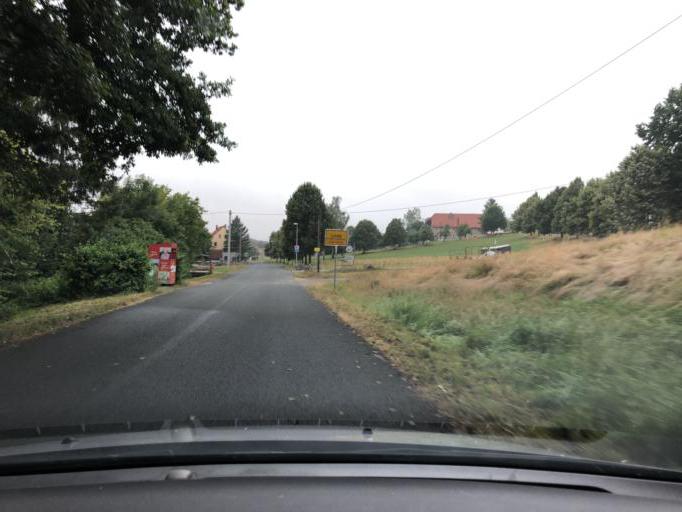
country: DE
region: Thuringia
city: Langenleuba-Niederhain
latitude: 50.9964
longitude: 12.6274
